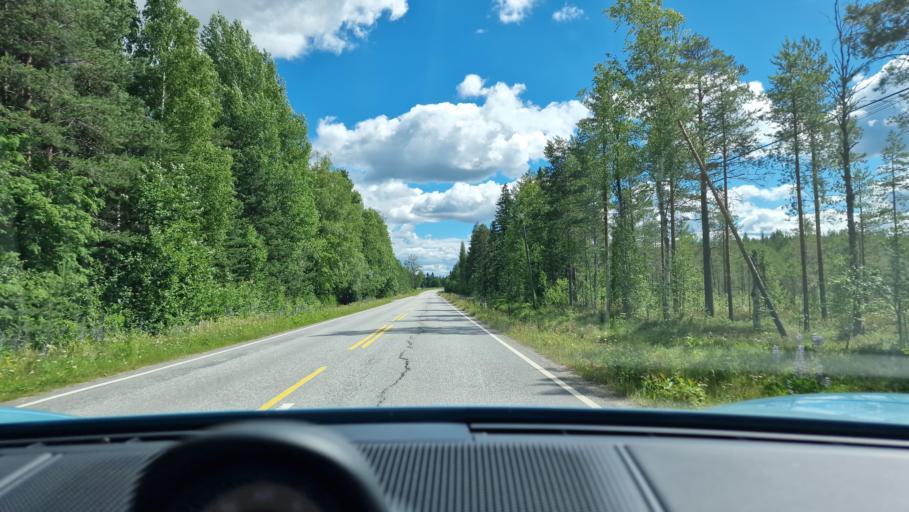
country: FI
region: Southern Ostrobothnia
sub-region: Jaerviseutu
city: Soini
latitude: 62.8333
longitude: 24.3346
